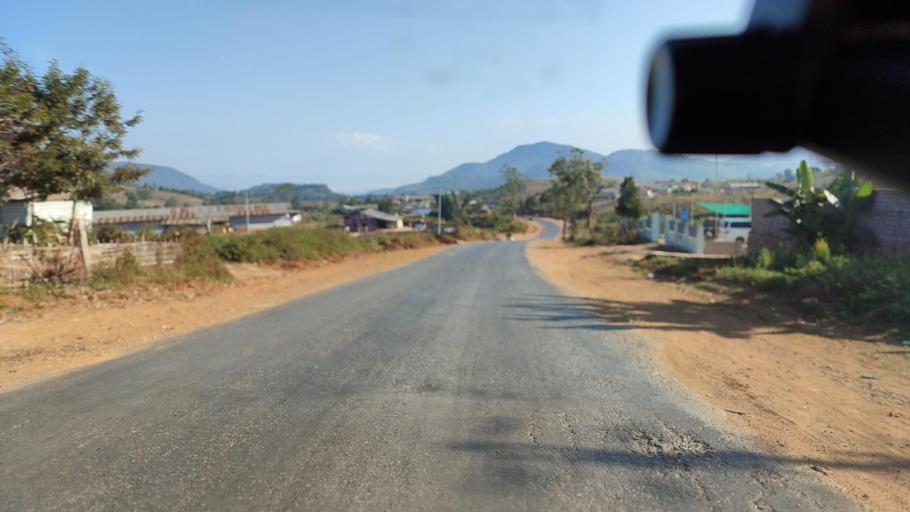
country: MM
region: Shan
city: Lashio
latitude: 23.0849
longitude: 97.8041
